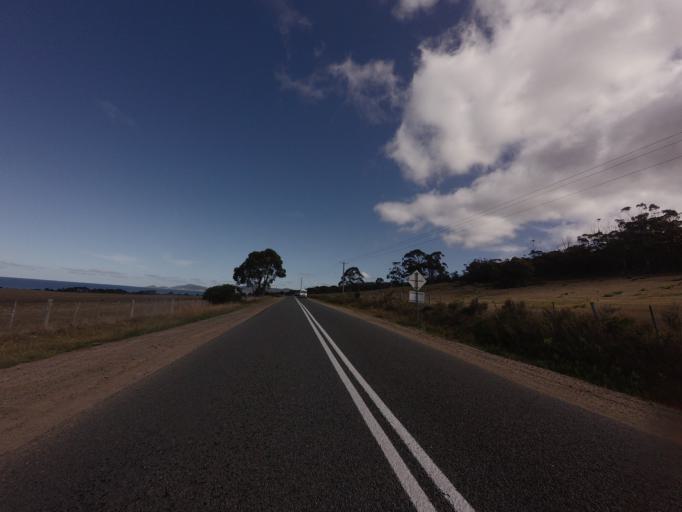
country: AU
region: Tasmania
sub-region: Break O'Day
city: St Helens
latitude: -41.7880
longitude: 148.2620
